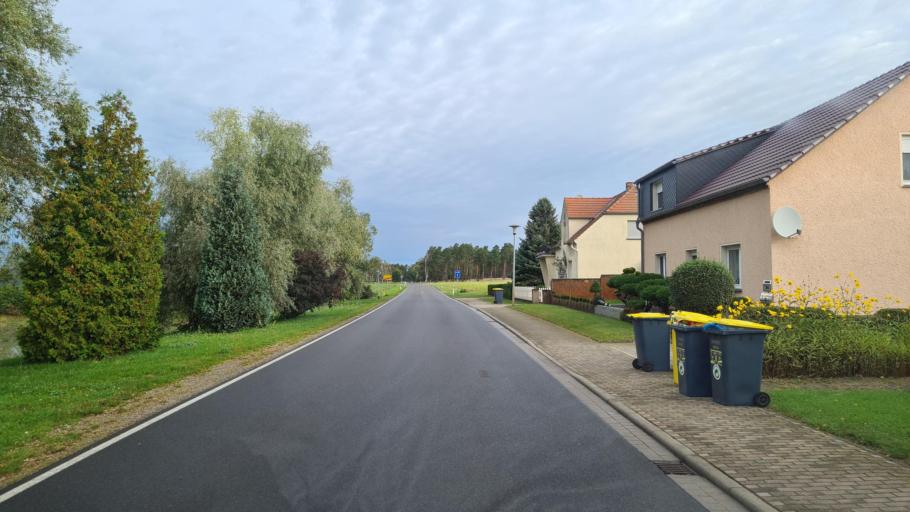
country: DE
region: Brandenburg
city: Kasel-Golzig
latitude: 51.9027
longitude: 13.7150
